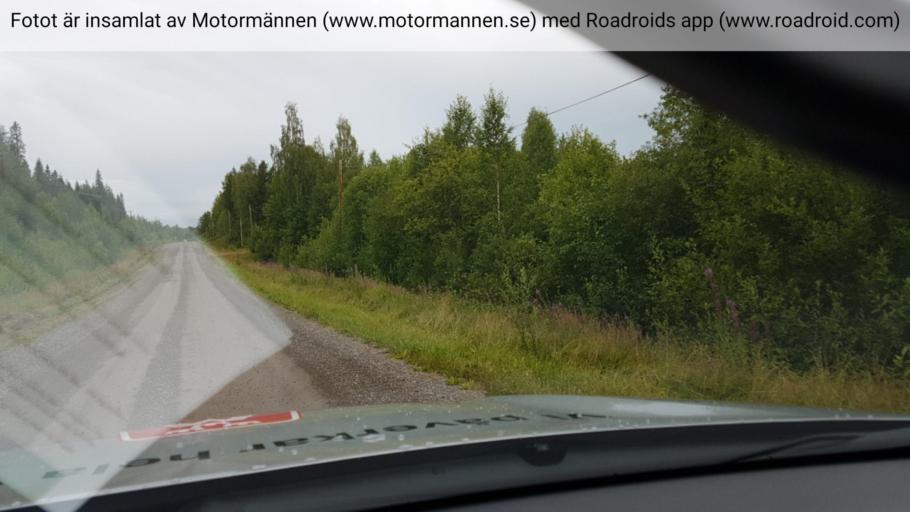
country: SE
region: Norrbotten
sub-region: Alvsbyns Kommun
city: AElvsbyn
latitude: 66.0022
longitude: 21.1436
